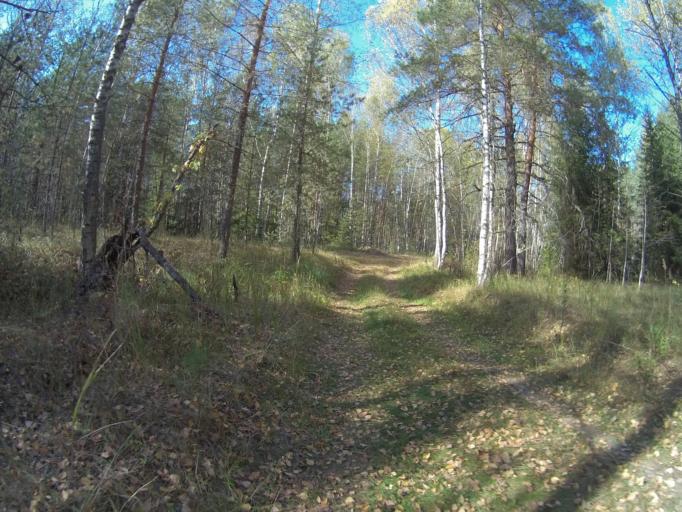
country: RU
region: Vladimir
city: Sobinka
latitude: 55.9238
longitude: 40.0668
